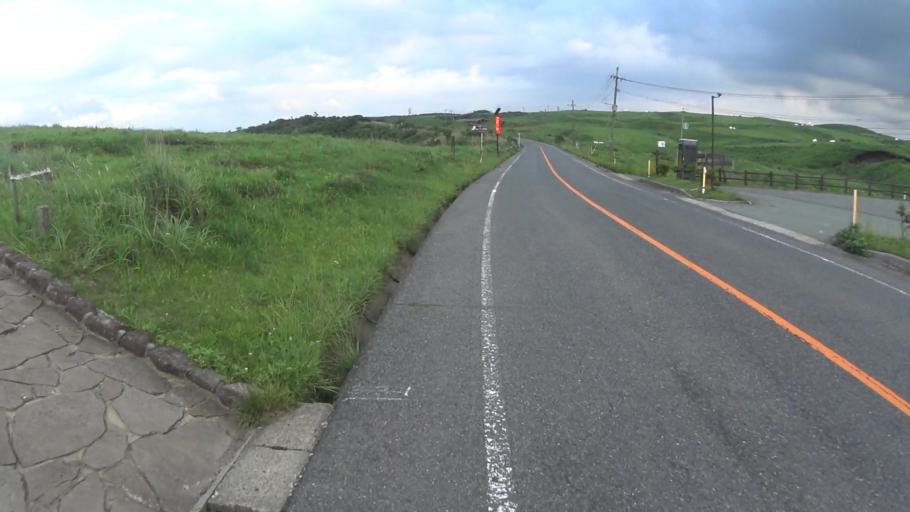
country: JP
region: Kumamoto
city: Aso
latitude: 32.9833
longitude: 131.0147
